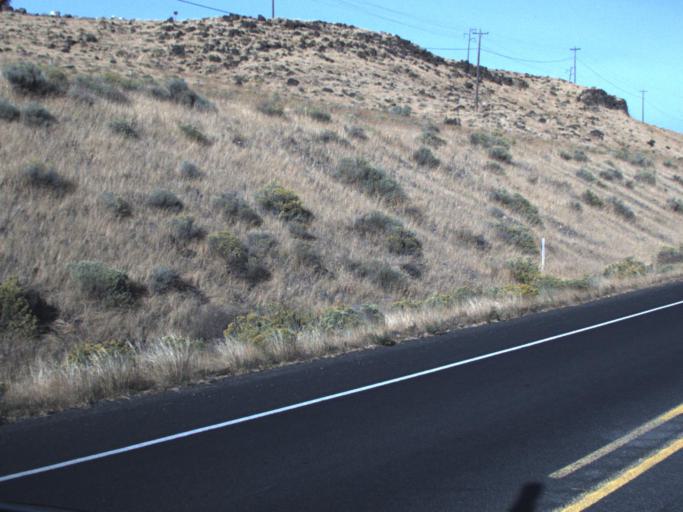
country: US
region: Oregon
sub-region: Morrow County
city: Boardman
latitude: 45.8663
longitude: -119.7760
